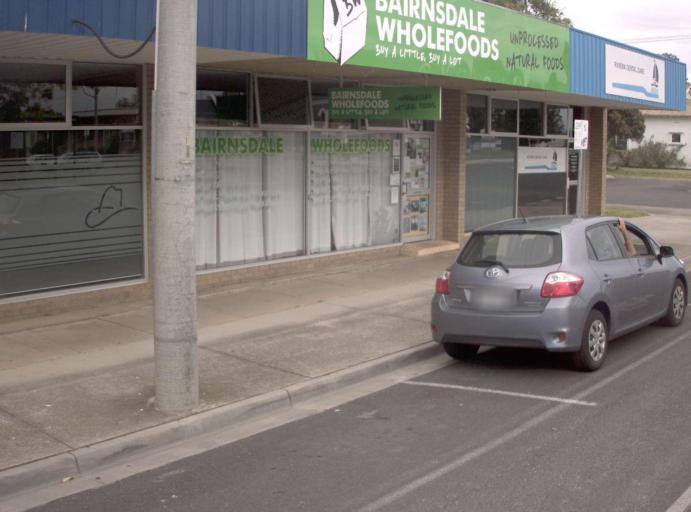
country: AU
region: Victoria
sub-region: East Gippsland
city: Bairnsdale
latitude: -37.8243
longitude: 147.6286
